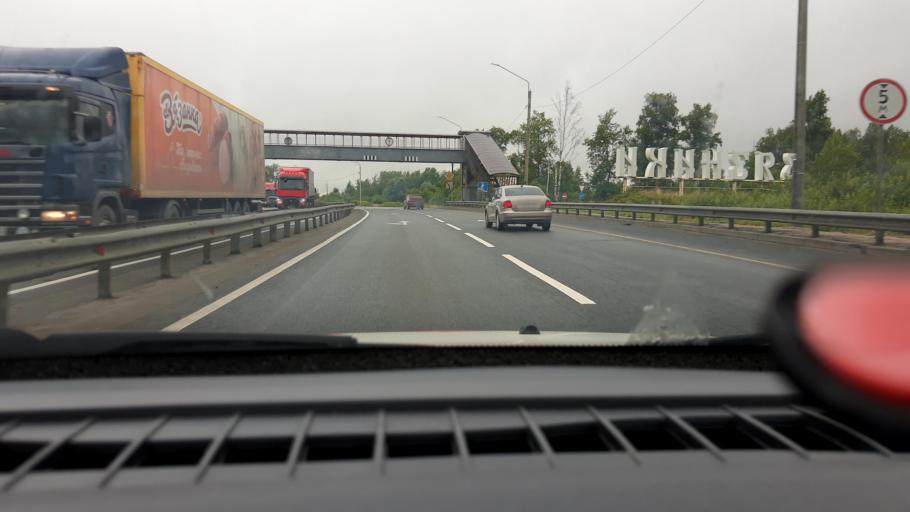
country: RU
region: Vladimir
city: Vyazniki
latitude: 56.2391
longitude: 42.1046
